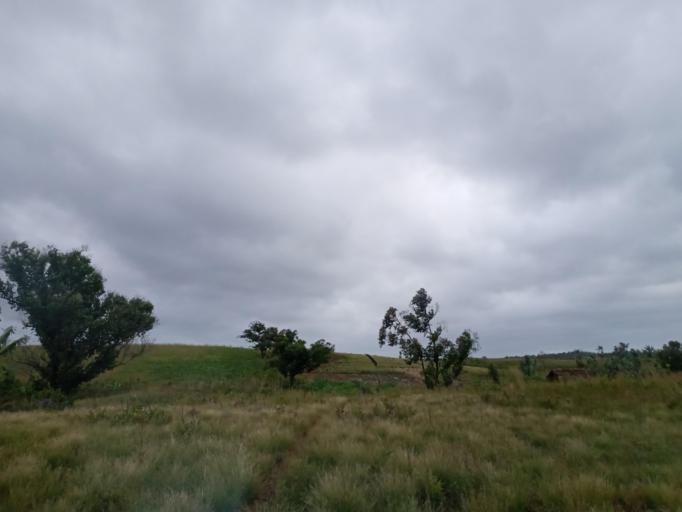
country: MG
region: Atsimo-Atsinanana
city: Vohipaho
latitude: -23.9092
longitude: 47.5187
